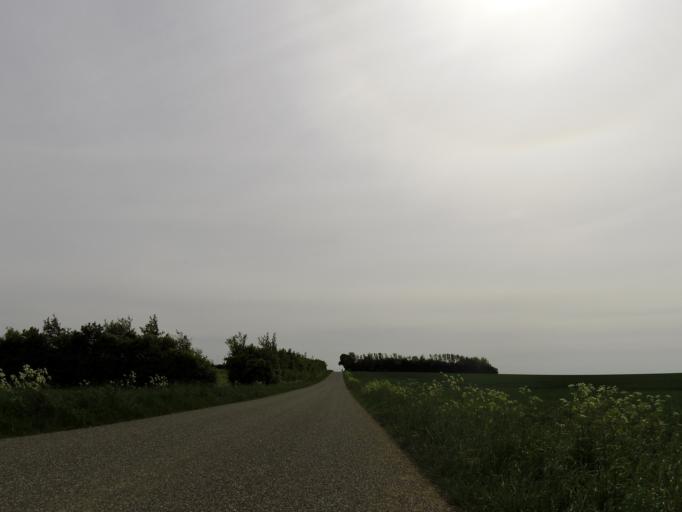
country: DK
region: Central Jutland
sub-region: Holstebro Kommune
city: Vinderup
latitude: 56.5802
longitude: 8.7717
